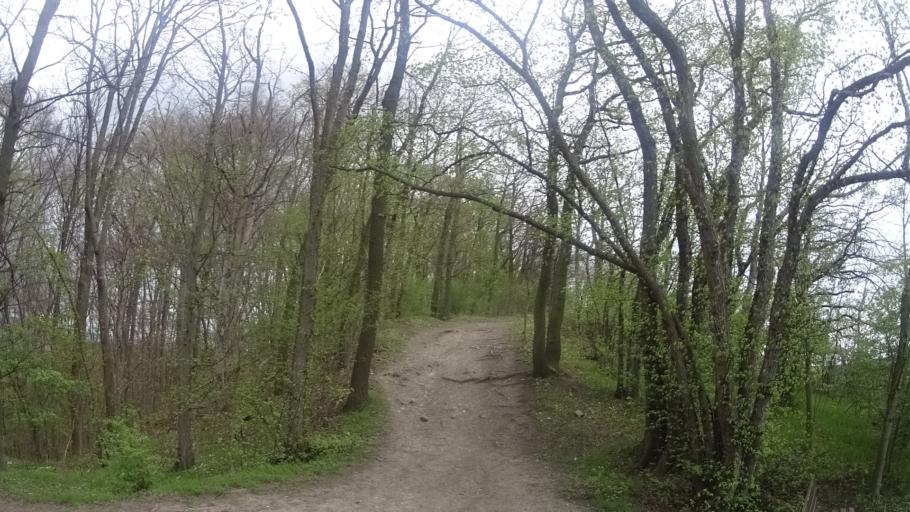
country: DE
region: Thuringia
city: Wandersleben
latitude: 50.8616
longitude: 10.8474
